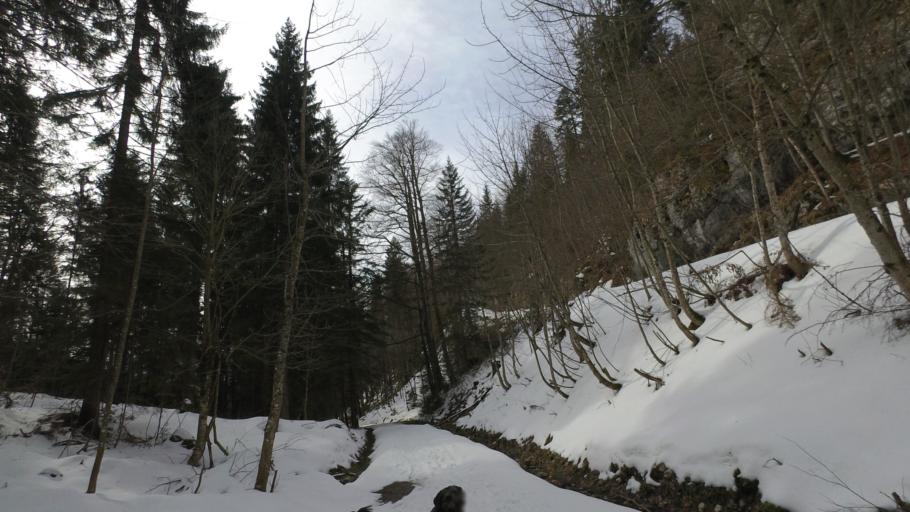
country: DE
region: Bavaria
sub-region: Upper Bavaria
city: Reit im Winkl
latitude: 47.6931
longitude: 12.4480
